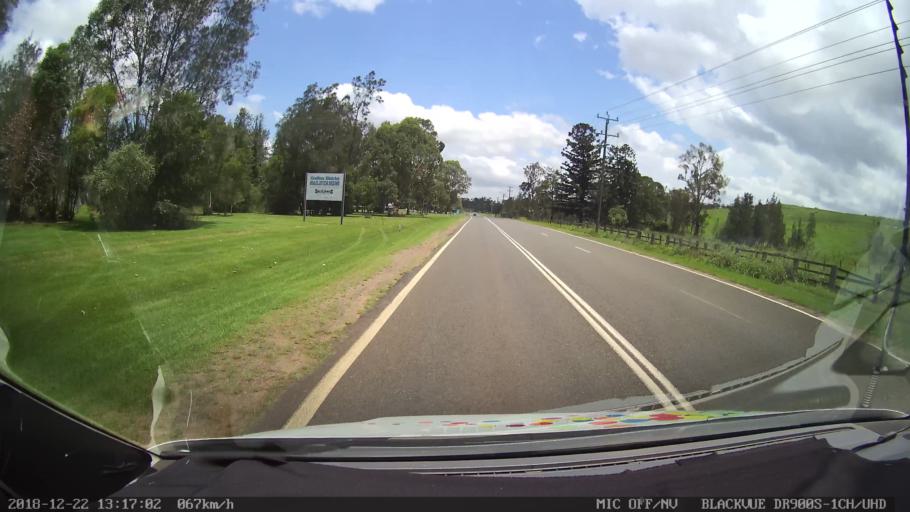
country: AU
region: New South Wales
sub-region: Clarence Valley
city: South Grafton
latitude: -29.7322
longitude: 152.9396
